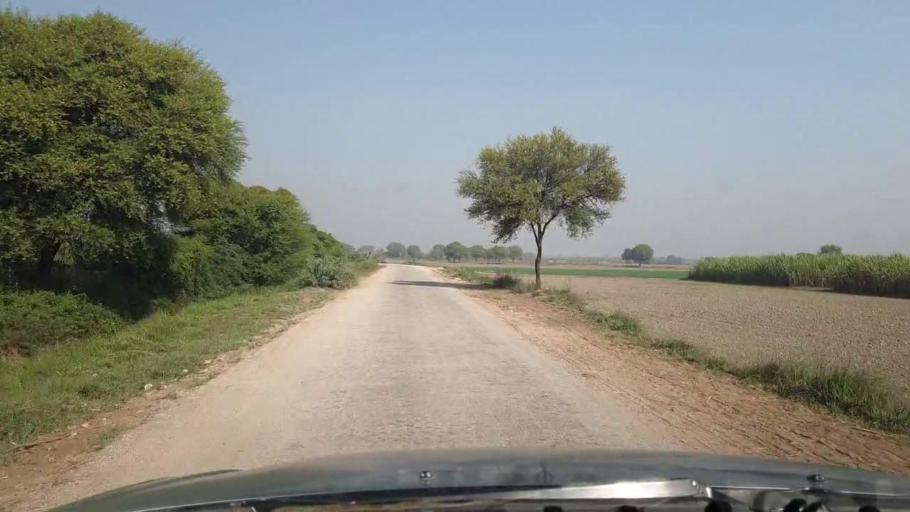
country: PK
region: Sindh
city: Tando Jam
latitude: 25.2979
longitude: 68.5338
